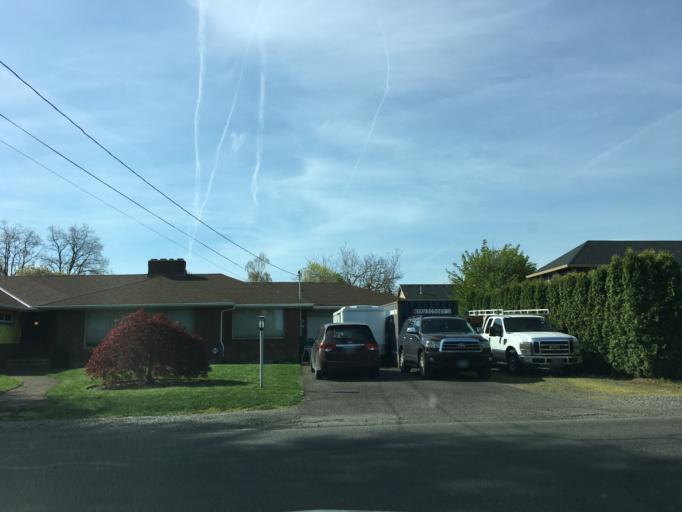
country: US
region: Oregon
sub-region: Multnomah County
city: Lents
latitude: 45.5373
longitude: -122.5233
